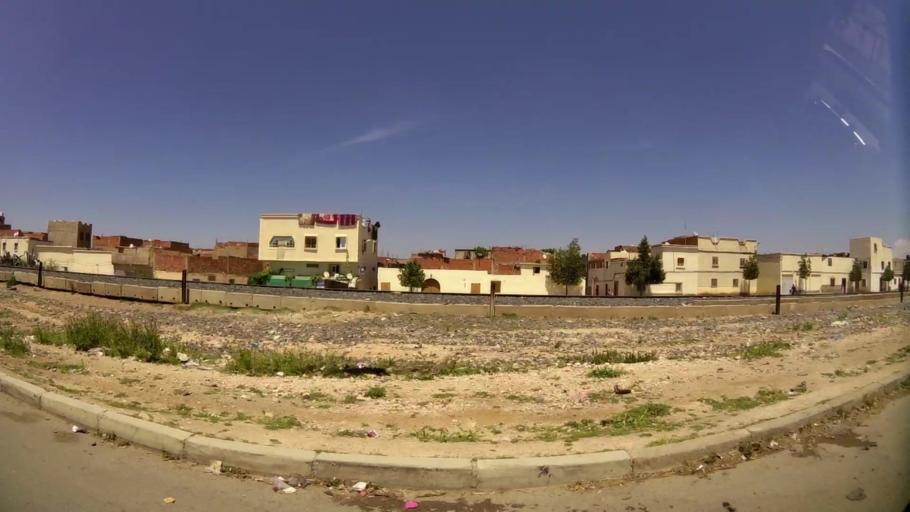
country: MA
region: Oriental
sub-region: Oujda-Angad
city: Oujda
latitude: 34.6947
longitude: -1.9462
